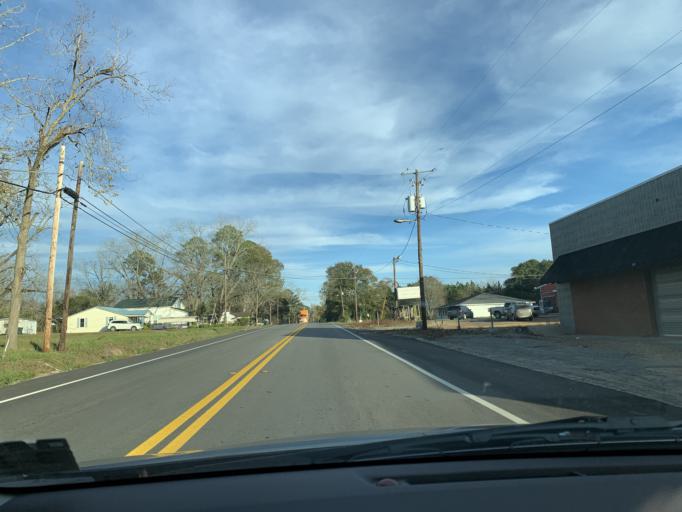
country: US
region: Georgia
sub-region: Irwin County
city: Ocilla
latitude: 31.5941
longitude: -83.2446
